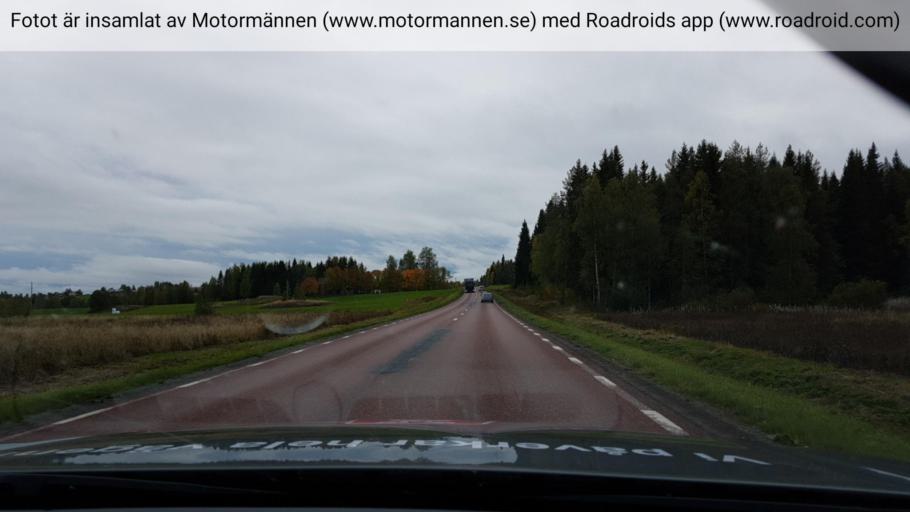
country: SE
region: Jaemtland
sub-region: Stroemsunds Kommun
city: Stroemsund
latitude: 63.7431
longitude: 15.4906
